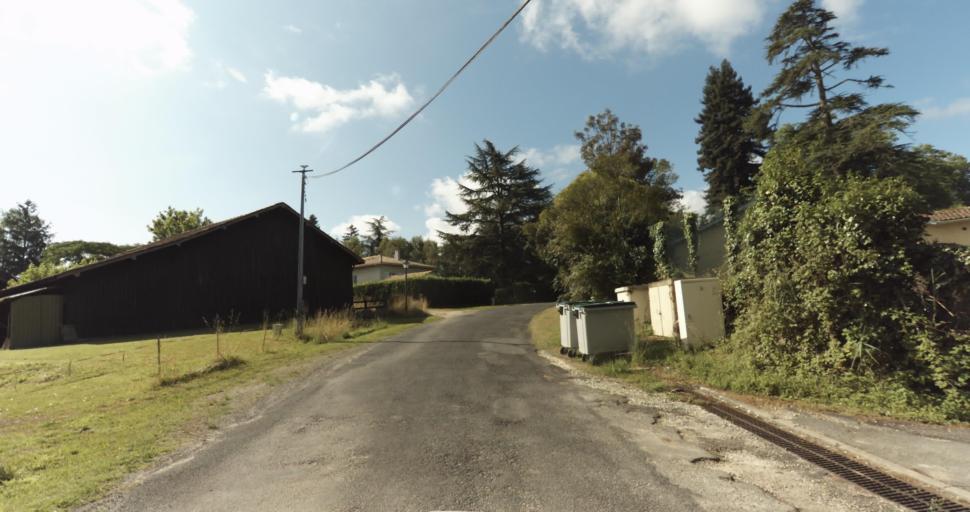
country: FR
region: Aquitaine
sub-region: Departement de la Gironde
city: Bazas
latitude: 44.4276
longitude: -0.2138
